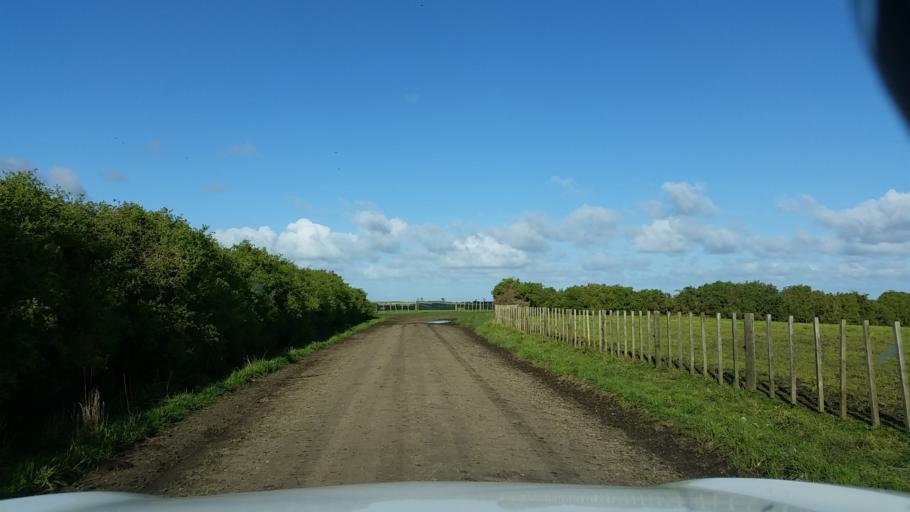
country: NZ
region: Taranaki
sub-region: South Taranaki District
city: Patea
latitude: -39.7547
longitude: 174.5224
